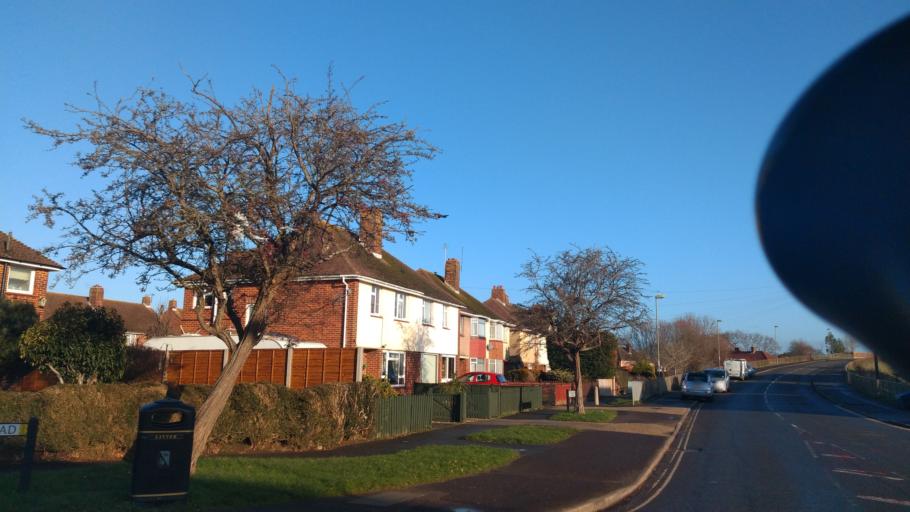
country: GB
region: England
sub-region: Hampshire
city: Fareham
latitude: 50.8275
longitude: -1.1760
